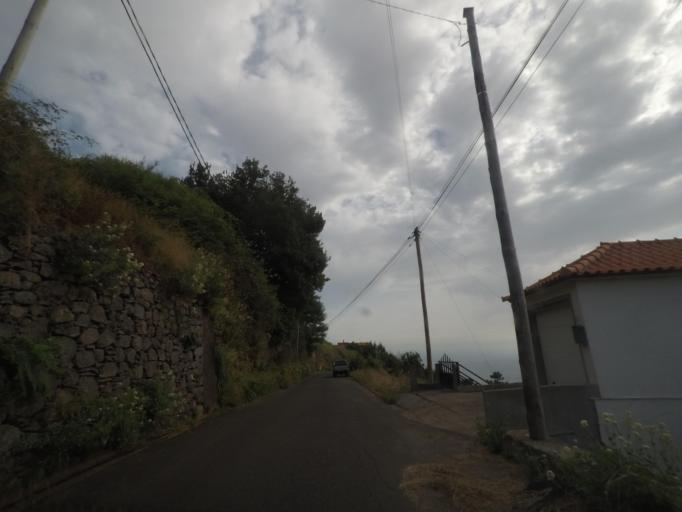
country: PT
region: Madeira
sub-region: Calheta
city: Arco da Calheta
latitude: 32.7341
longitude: -17.1544
